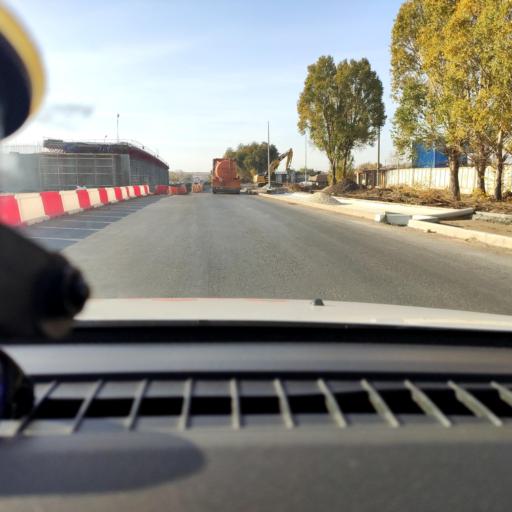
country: RU
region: Samara
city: Samara
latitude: 53.1042
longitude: 50.0776
